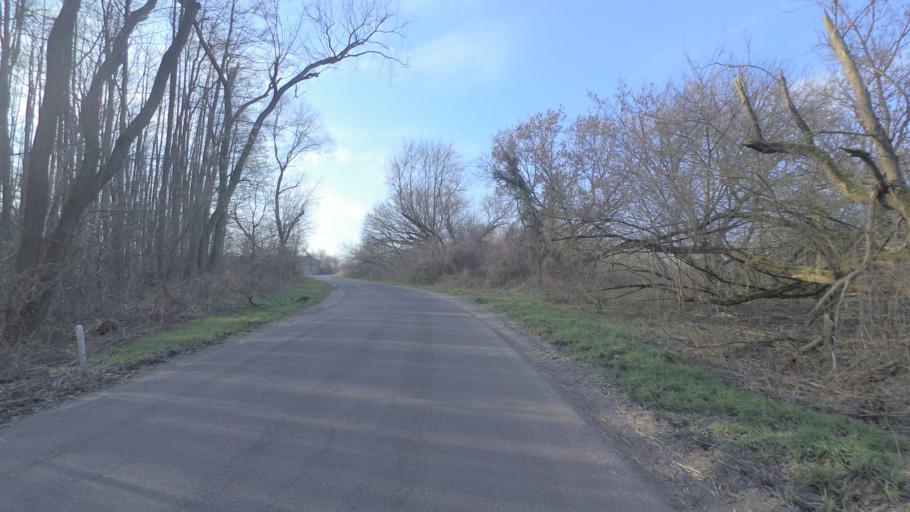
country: DE
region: Brandenburg
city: Rangsdorf
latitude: 52.2740
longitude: 13.4424
